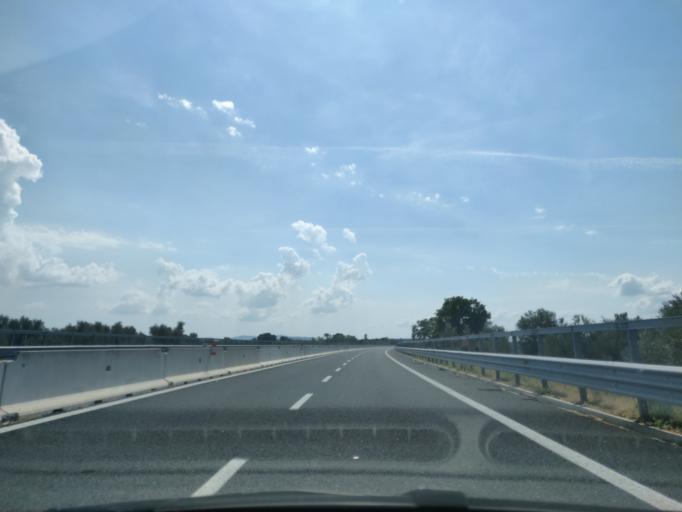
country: IT
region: Latium
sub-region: Provincia di Viterbo
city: Blera
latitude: 42.3217
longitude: 11.9900
